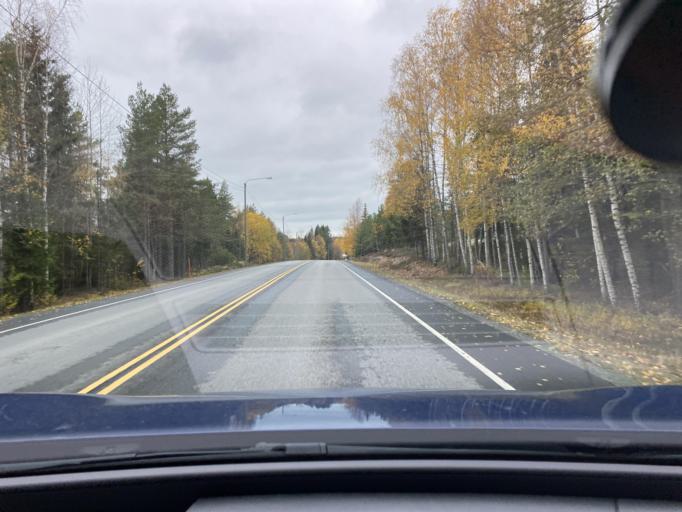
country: FI
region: Satakunta
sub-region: Rauma
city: Rauma
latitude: 61.1267
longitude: 21.6100
